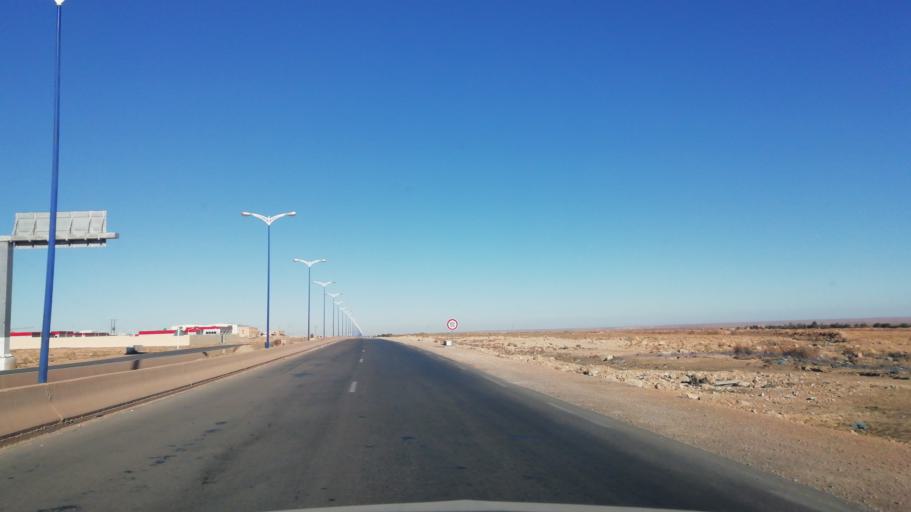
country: DZ
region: Wilaya de Naama
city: Naama
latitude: 33.5428
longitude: -0.2526
